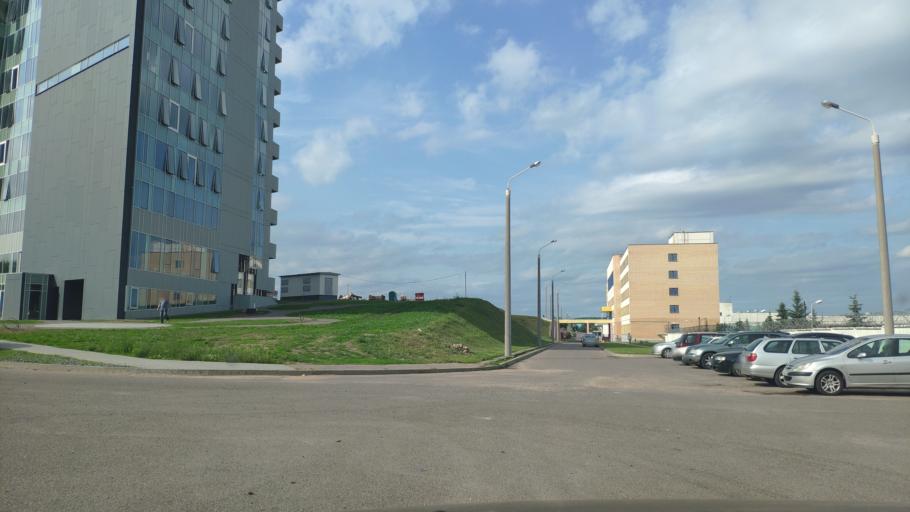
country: BY
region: Minsk
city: Vyaliki Trastsyanets
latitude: 53.8633
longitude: 27.6886
